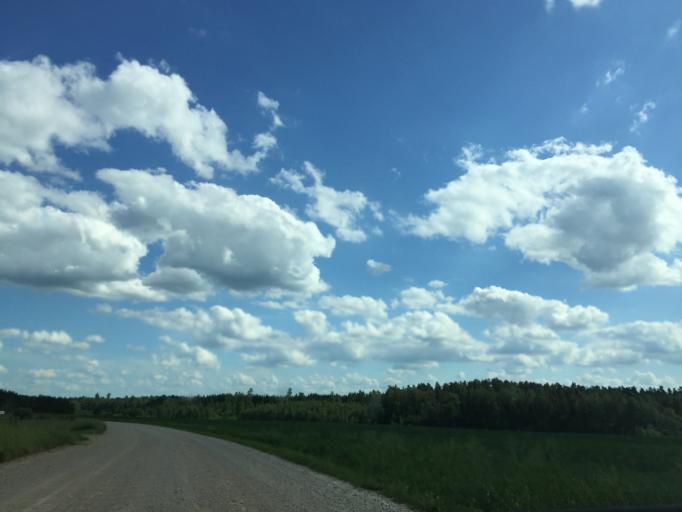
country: LV
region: Jaunpils
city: Jaunpils
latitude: 56.8144
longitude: 23.0721
